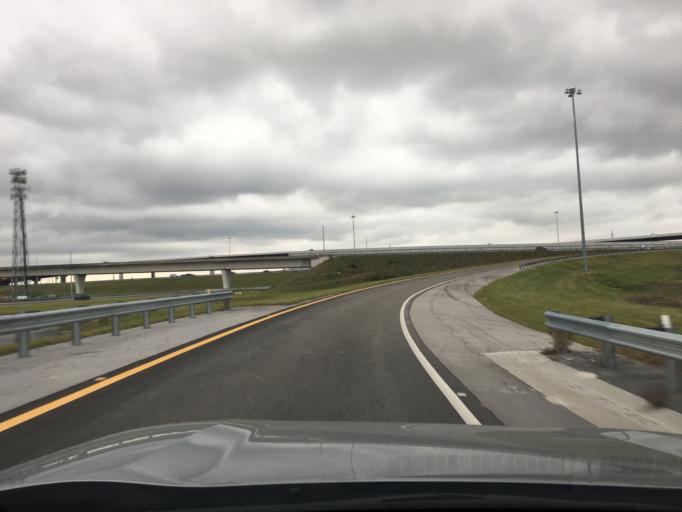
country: US
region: Florida
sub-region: Miami-Dade County
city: Palm Springs North
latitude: 25.9519
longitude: -80.3482
